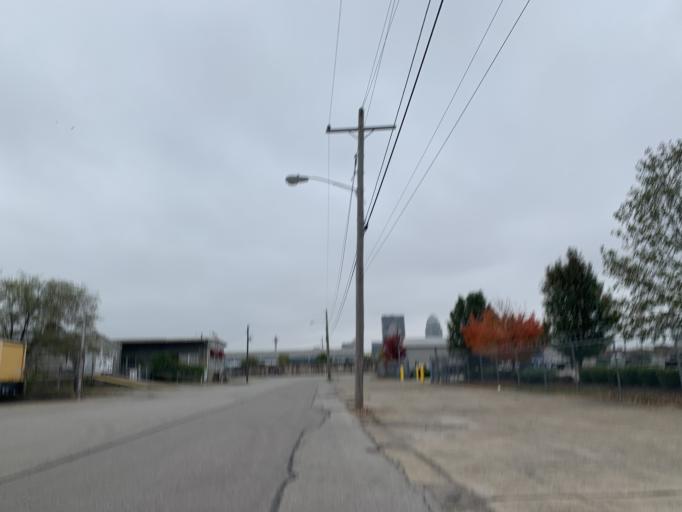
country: US
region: Kentucky
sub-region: Jefferson County
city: Louisville
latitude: 38.2599
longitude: -85.7742
